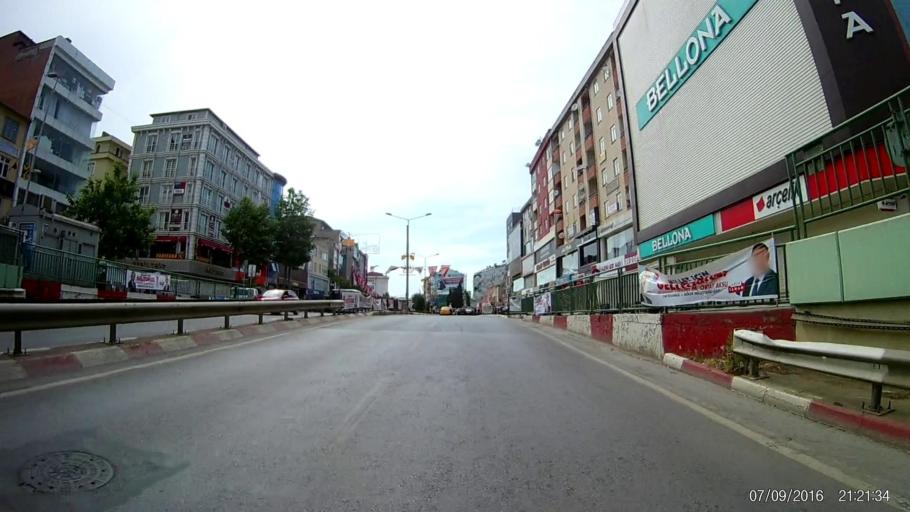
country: TR
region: Istanbul
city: Sultanbeyli
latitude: 40.9682
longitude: 29.2632
